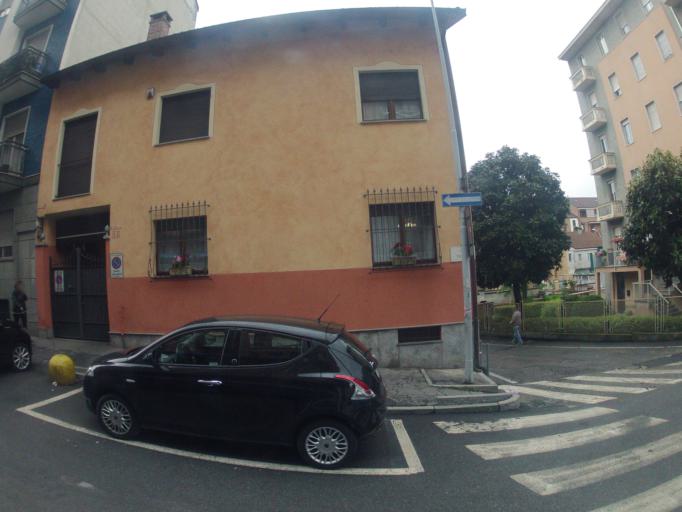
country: IT
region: Piedmont
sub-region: Provincia di Torino
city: Nichelino
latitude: 45.0163
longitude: 7.6630
